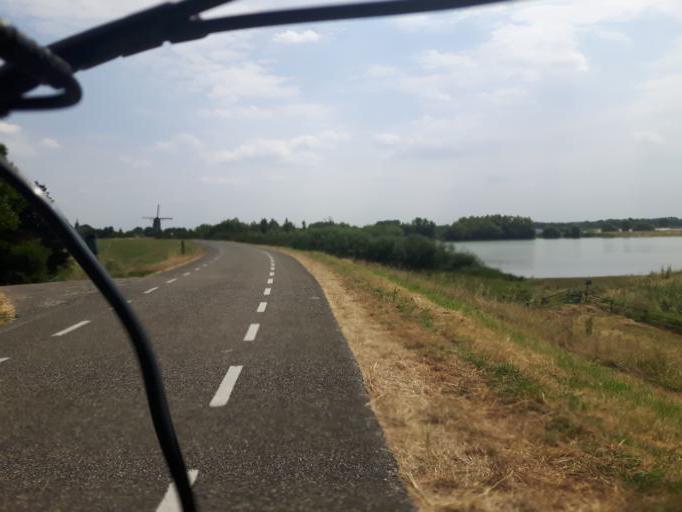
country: NL
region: Gelderland
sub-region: Gemeente Zaltbommel
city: Zaltbommel
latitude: 51.8170
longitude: 5.2054
